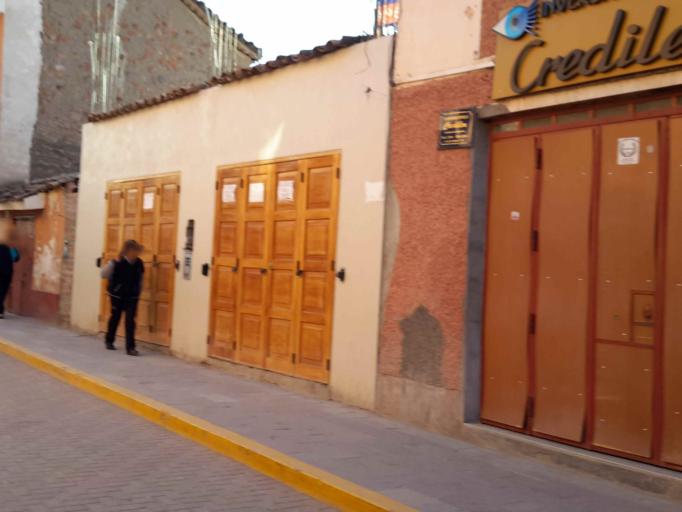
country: PE
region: Ayacucho
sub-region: Provincia de Huamanga
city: Ayacucho
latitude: -13.1569
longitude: -74.2256
